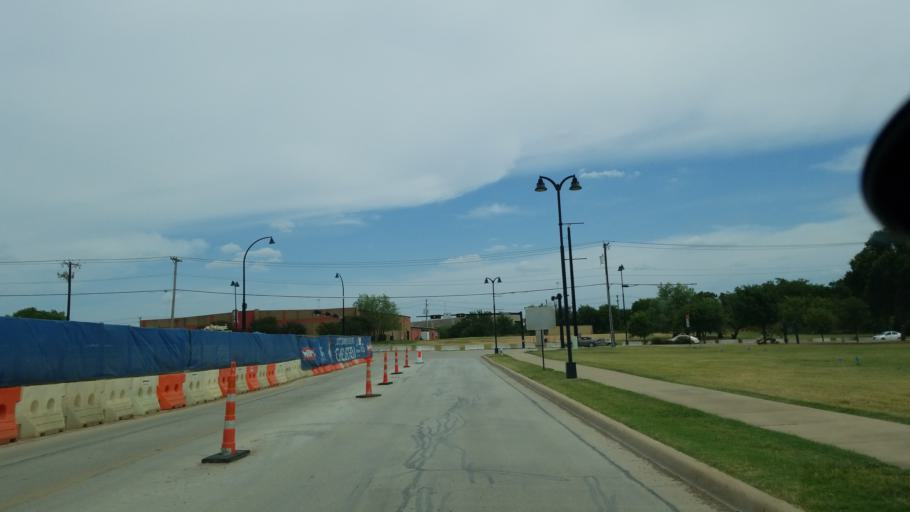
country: US
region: Texas
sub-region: Tarrant County
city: Arlington
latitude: 32.7457
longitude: -97.0840
